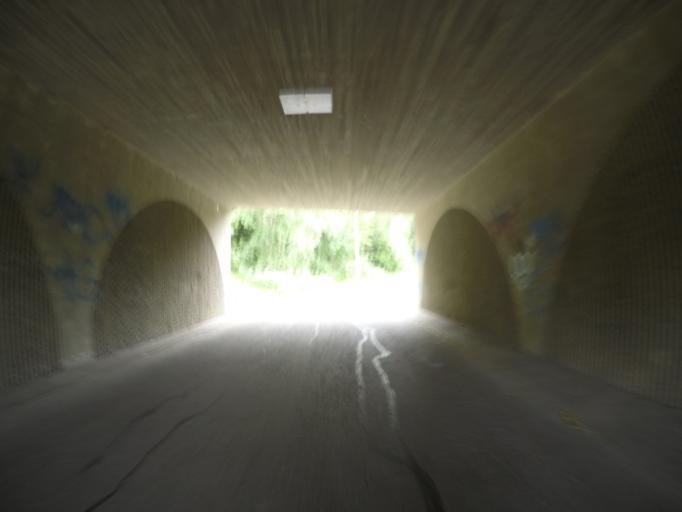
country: FI
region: Haeme
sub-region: Haemeenlinna
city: Haemeenlinna
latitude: 60.9961
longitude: 24.4941
